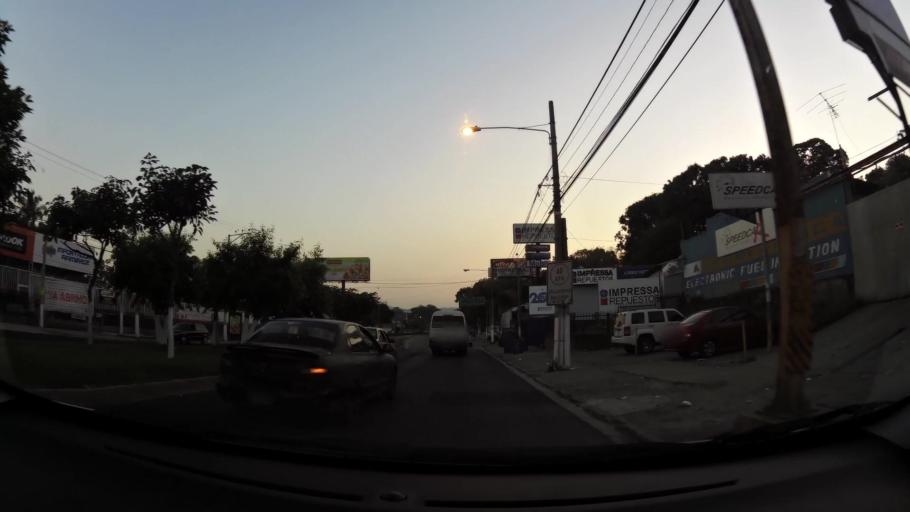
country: SV
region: San Salvador
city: Mejicanos
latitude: 13.7101
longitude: -89.2258
